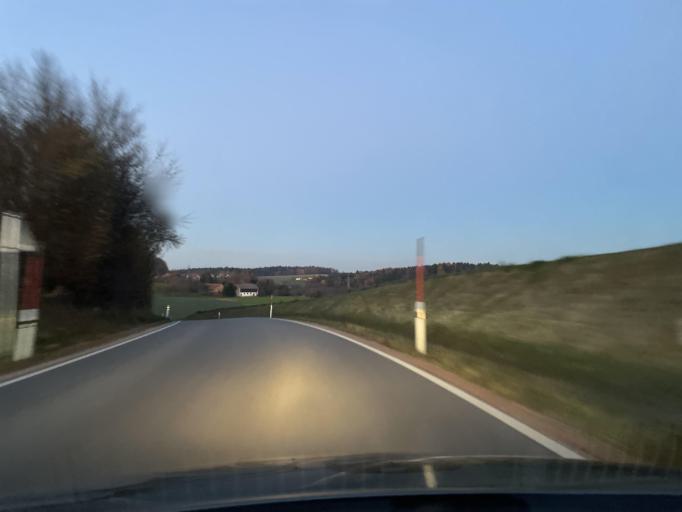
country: DE
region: Bavaria
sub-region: Lower Bavaria
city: Reut
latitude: 48.3072
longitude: 12.9510
